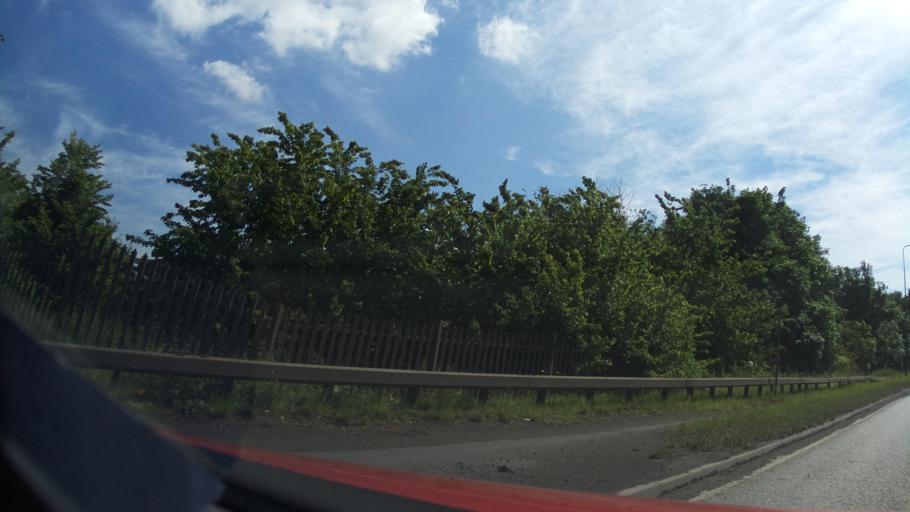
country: GB
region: England
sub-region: North Lincolnshire
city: Bottesford
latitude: 53.5640
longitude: -0.6056
